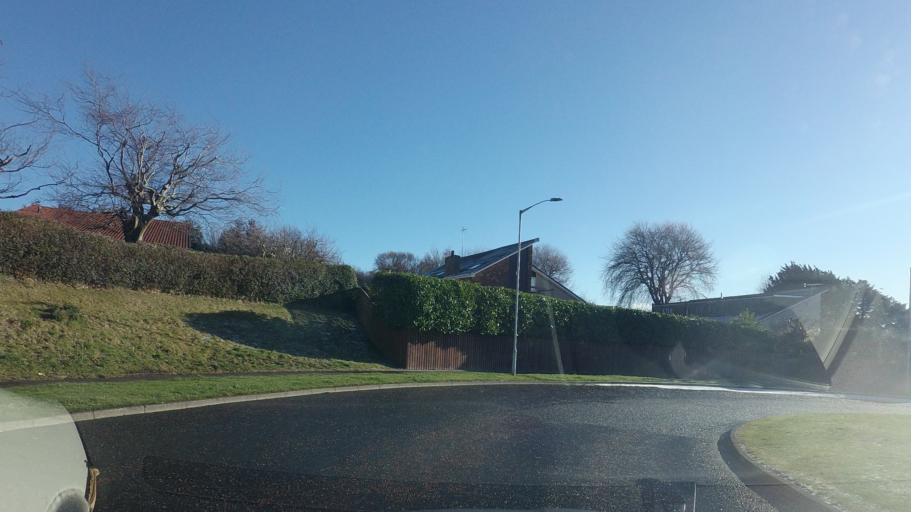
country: GB
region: Scotland
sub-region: Fife
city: Aberdour
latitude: 56.0423
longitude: -3.3371
